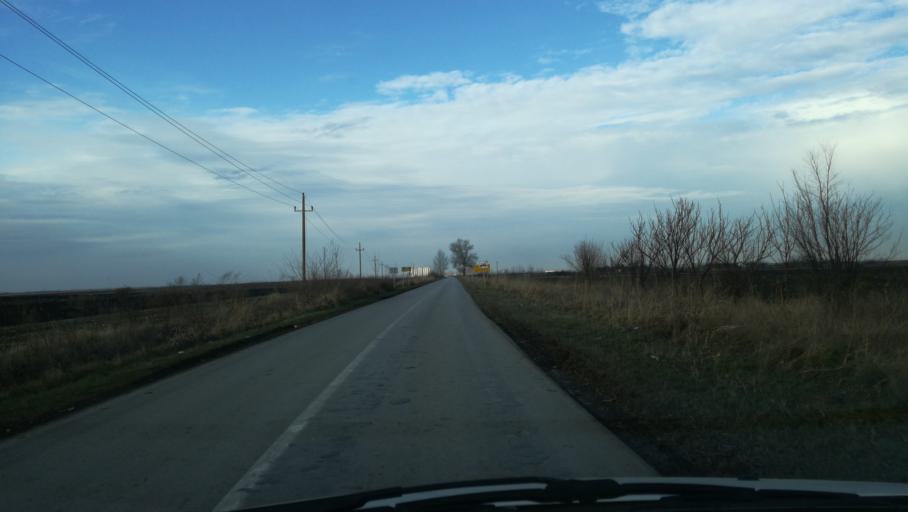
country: RS
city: Novi Kozarci
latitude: 45.7843
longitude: 20.6217
